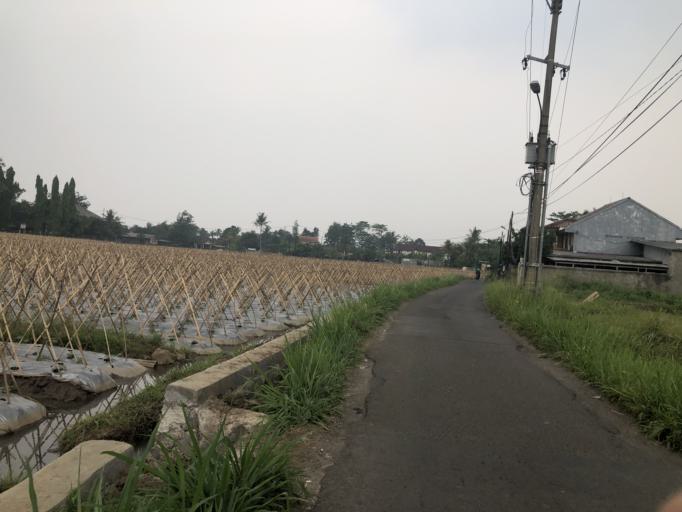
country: ID
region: West Java
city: Ciampea
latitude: -6.5662
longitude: 106.7458
